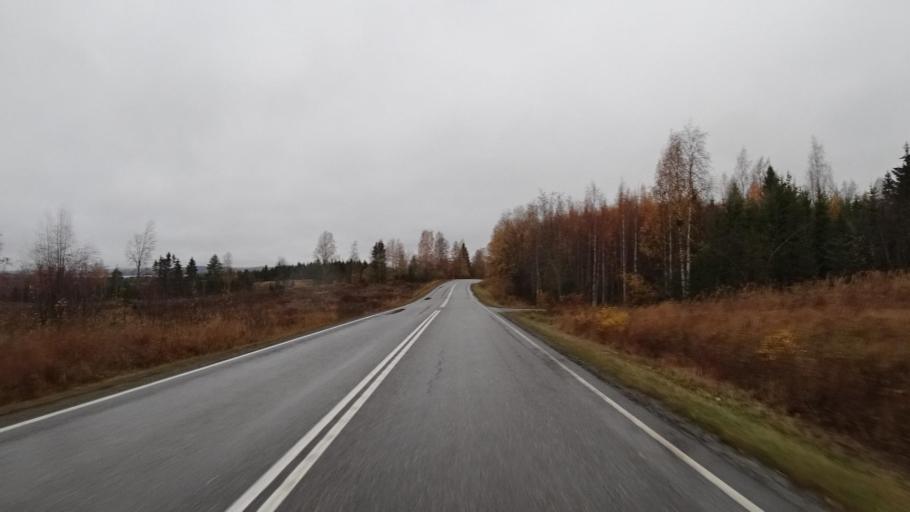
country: FI
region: Northern Savo
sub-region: Koillis-Savo
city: Tuusniemi
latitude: 62.7896
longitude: 28.5786
